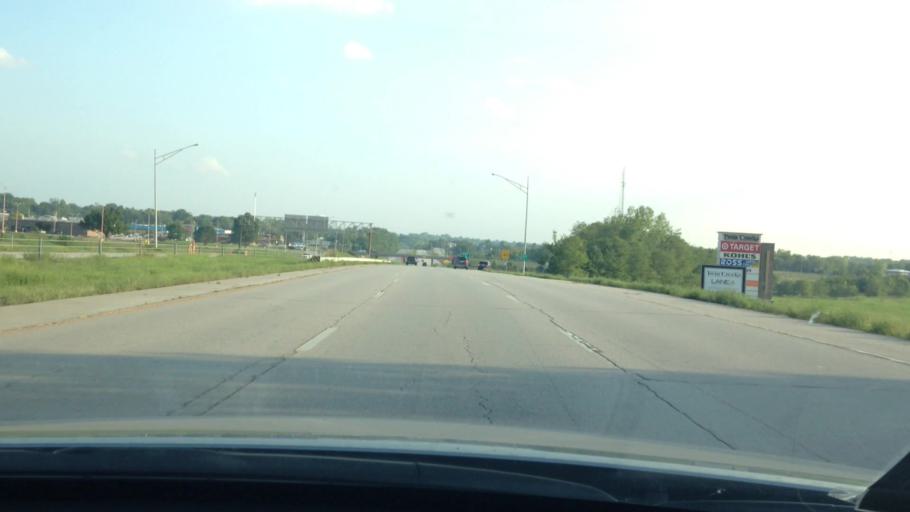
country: US
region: Missouri
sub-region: Clay County
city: Gladstone
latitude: 39.2516
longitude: -94.5904
